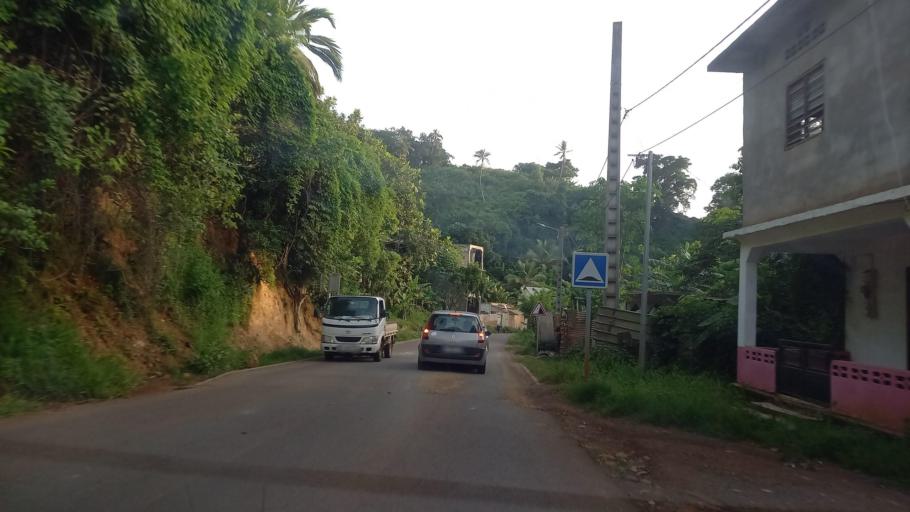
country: YT
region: M'Tsangamouji
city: M'Tsangamouji
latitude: -12.7601
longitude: 45.0887
